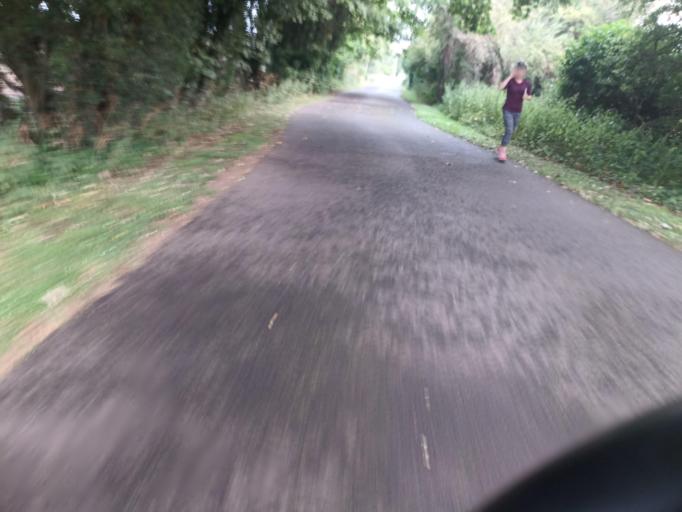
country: GB
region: Northern Ireland
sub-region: Castlereagh District
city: Dundonald
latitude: 54.5815
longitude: -5.7899
